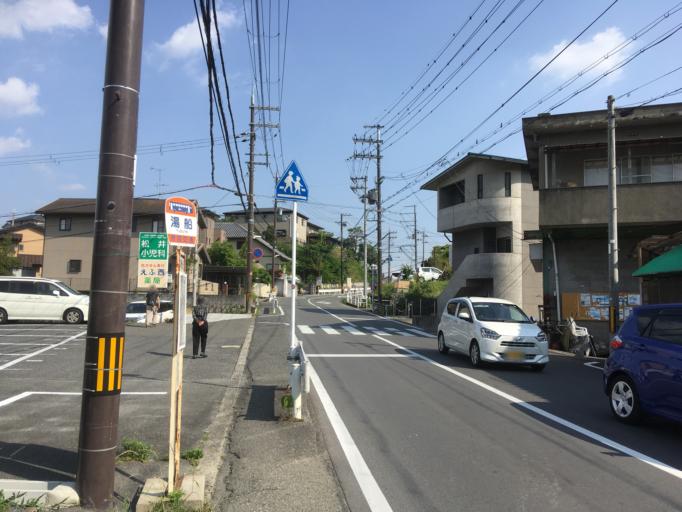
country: JP
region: Nara
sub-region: Ikoma-shi
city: Ikoma
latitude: 34.6868
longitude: 135.7013
